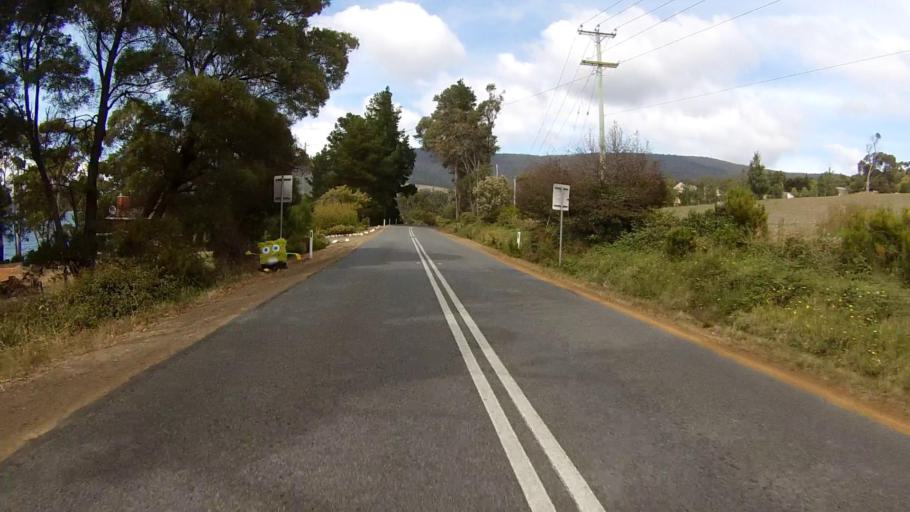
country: AU
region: Tasmania
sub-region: Kingborough
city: Kettering
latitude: -43.1679
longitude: 147.2438
